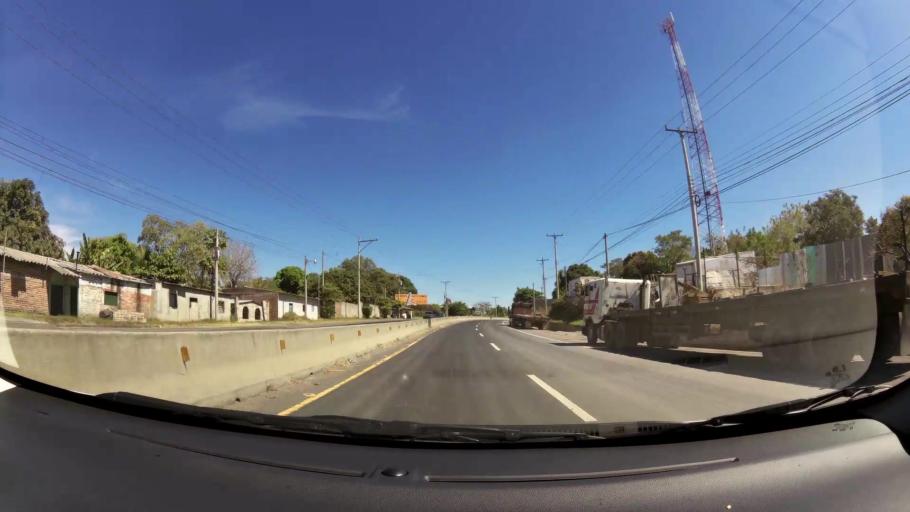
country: SV
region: La Libertad
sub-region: Distrito de Quezaltepeque
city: Quezaltepeque
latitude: 13.8162
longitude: -89.3104
